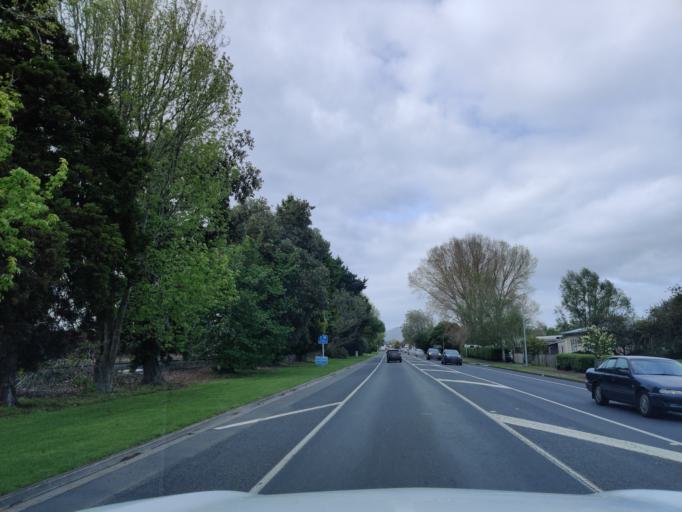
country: NZ
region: Waikato
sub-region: Waikato District
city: Ngaruawahia
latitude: -37.5460
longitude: 175.1584
